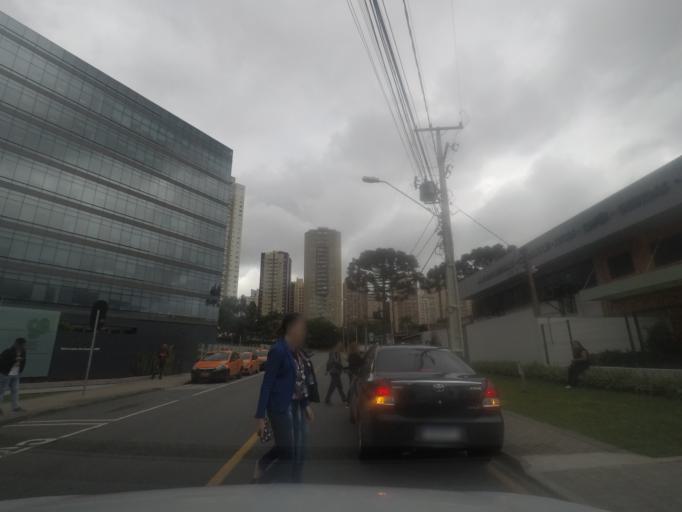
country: BR
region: Parana
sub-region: Curitiba
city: Curitiba
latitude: -25.4387
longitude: -49.2405
